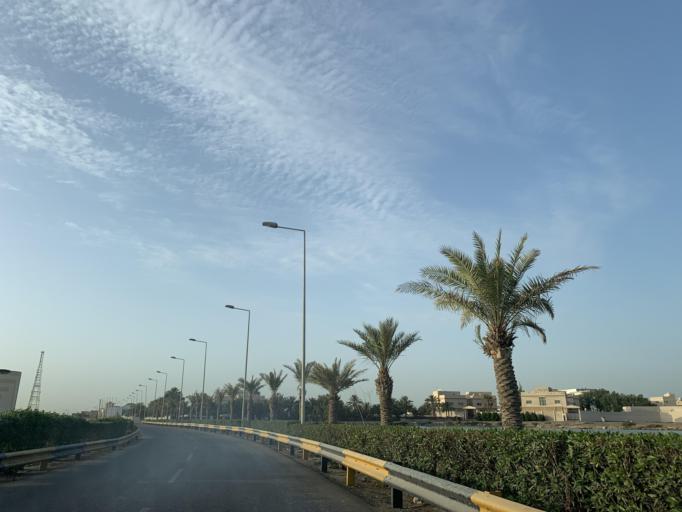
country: BH
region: Manama
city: Manama
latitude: 26.1884
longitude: 50.5853
